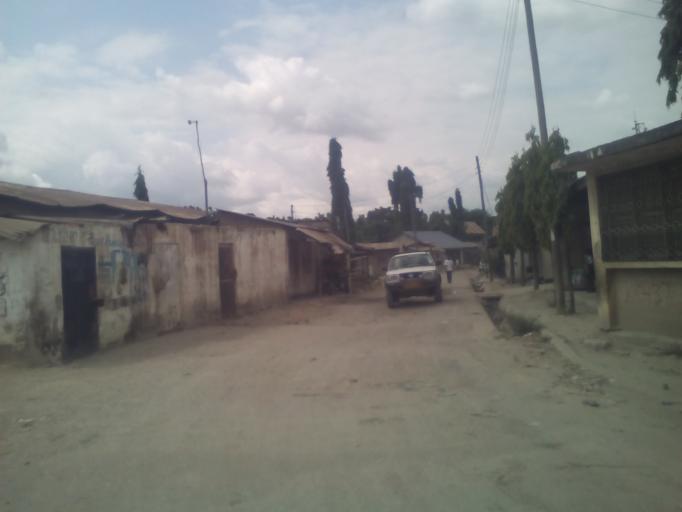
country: TZ
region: Dar es Salaam
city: Dar es Salaam
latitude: -6.8555
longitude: 39.2431
